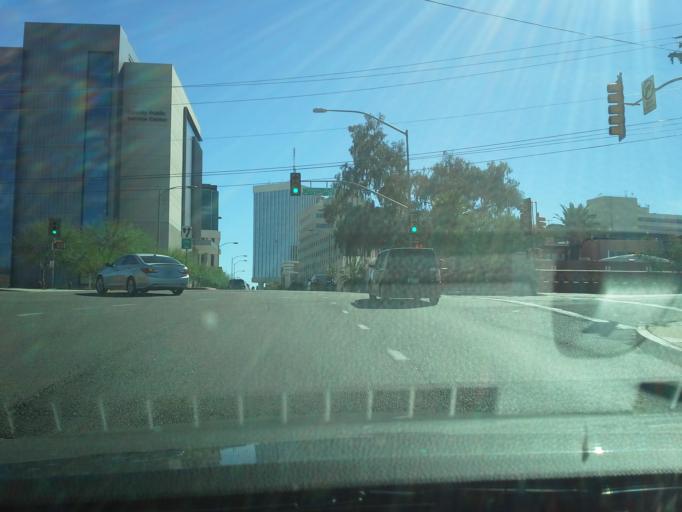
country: US
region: Arizona
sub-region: Pima County
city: South Tucson
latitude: 32.2266
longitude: -110.9718
